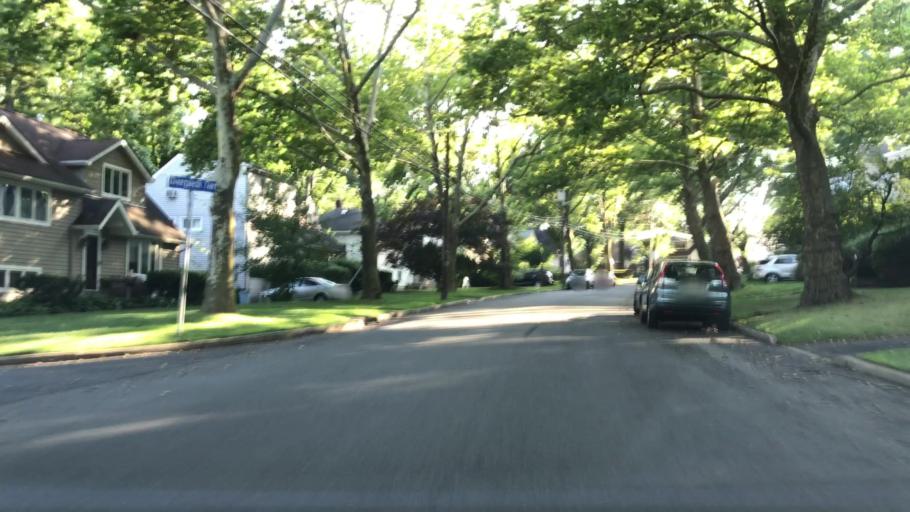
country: US
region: New Jersey
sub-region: Bergen County
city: Teaneck
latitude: 40.8840
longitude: -73.9986
